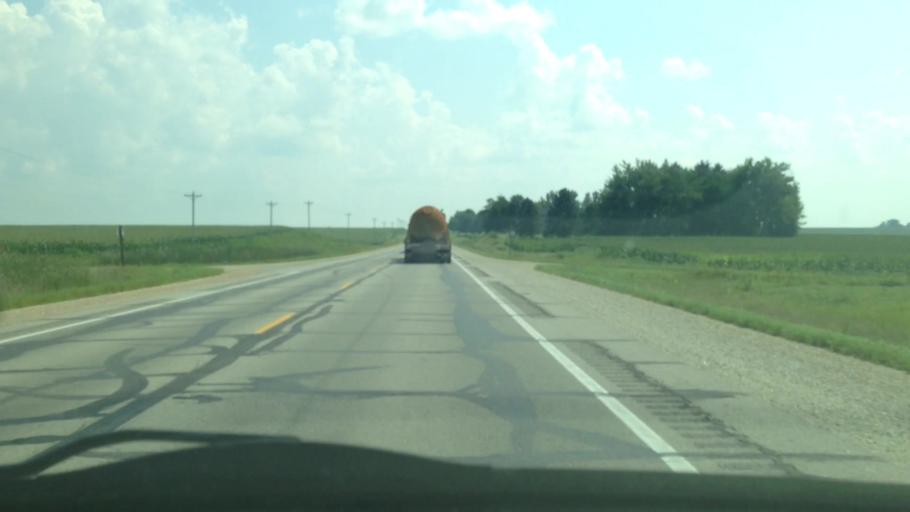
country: US
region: Iowa
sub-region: Chickasaw County
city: New Hampton
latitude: 43.1560
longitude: -92.2989
